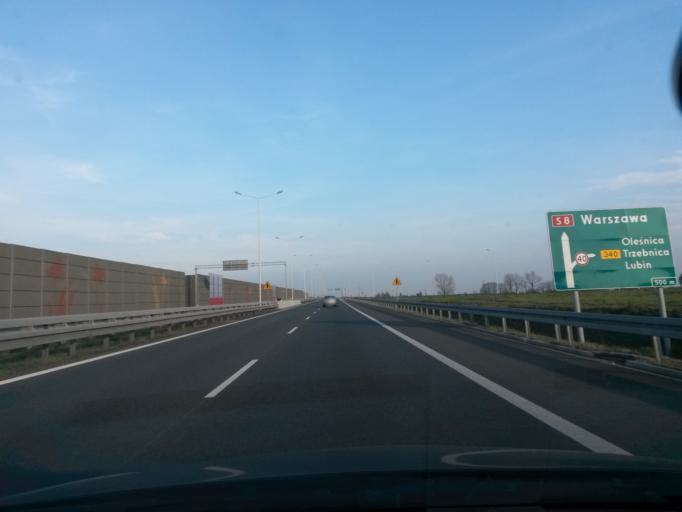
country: PL
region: Lower Silesian Voivodeship
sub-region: Powiat olesnicki
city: Olesnica
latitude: 51.2273
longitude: 17.3603
